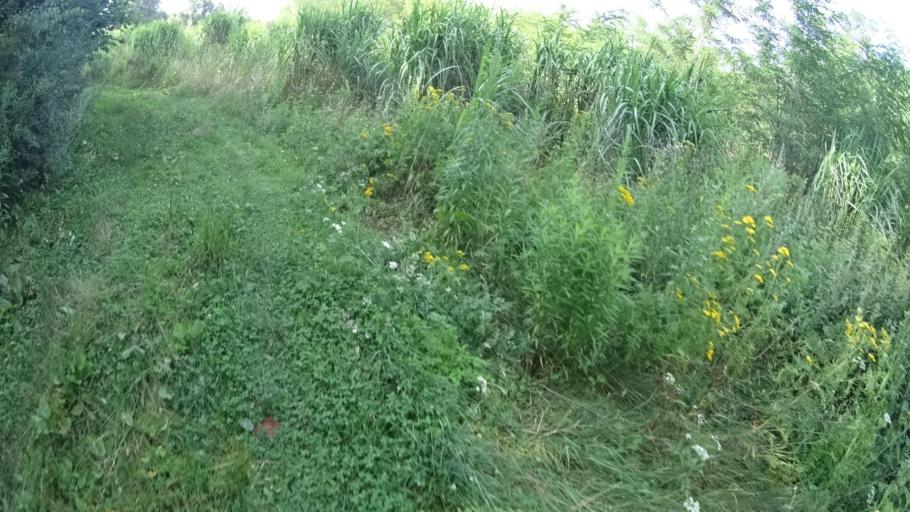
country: PL
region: Masovian Voivodeship
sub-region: Powiat piaseczynski
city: Lesznowola
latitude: 52.0270
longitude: 20.9043
